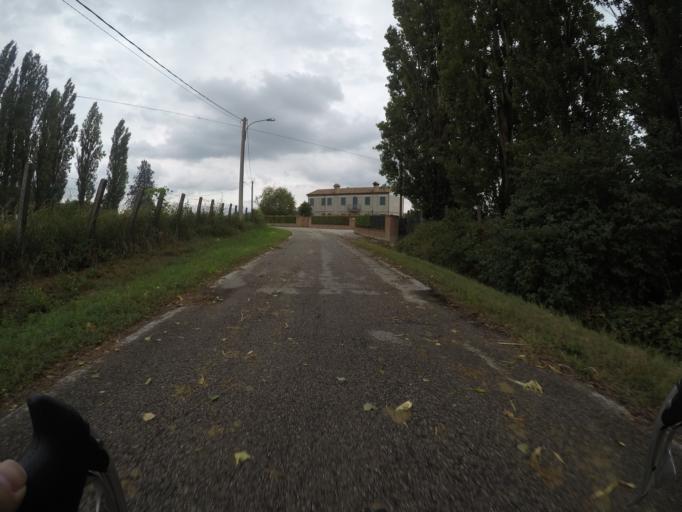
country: IT
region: Veneto
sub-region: Provincia di Rovigo
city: Polesella
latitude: 44.9604
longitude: 11.7294
